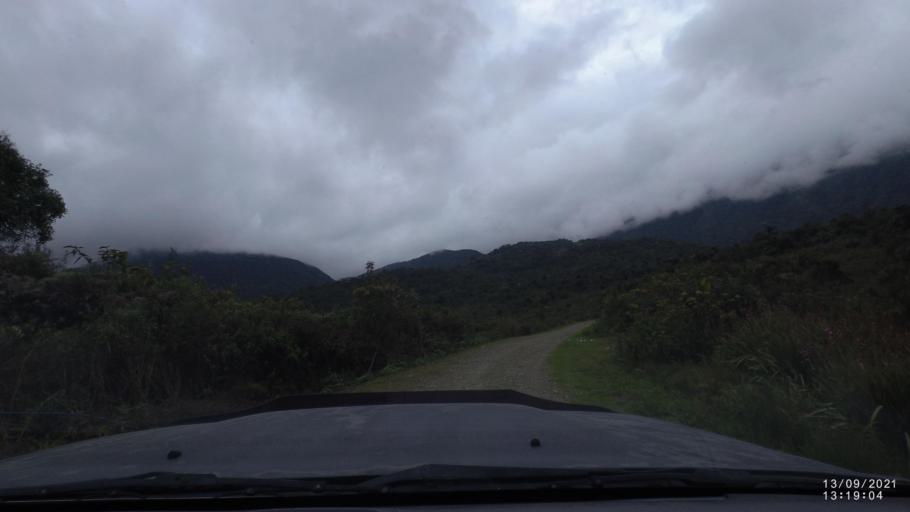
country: BO
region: Cochabamba
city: Colomi
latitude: -17.2046
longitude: -65.8628
